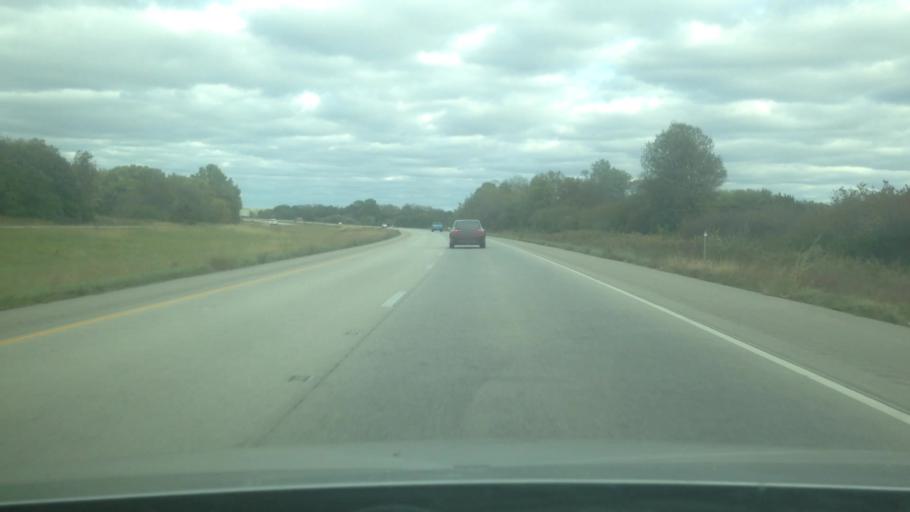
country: US
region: Illinois
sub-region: Macon County
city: Forsyth
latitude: 39.9108
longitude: -88.8780
